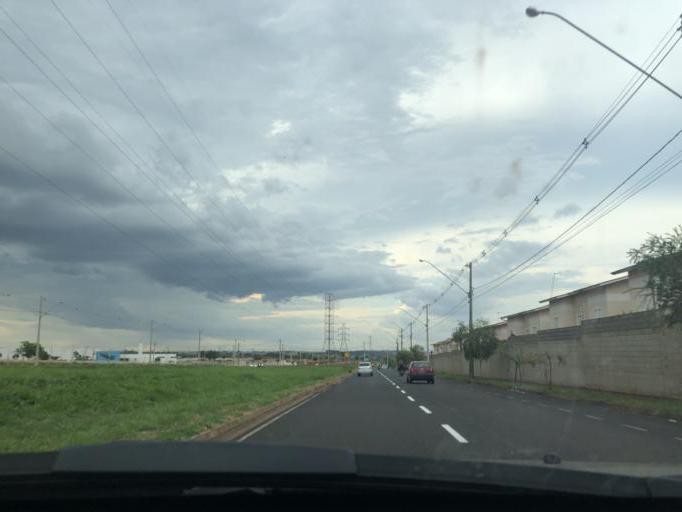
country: BR
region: Sao Paulo
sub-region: Sao Jose Do Rio Preto
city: Sao Jose do Rio Preto
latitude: -20.8392
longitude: -49.4180
